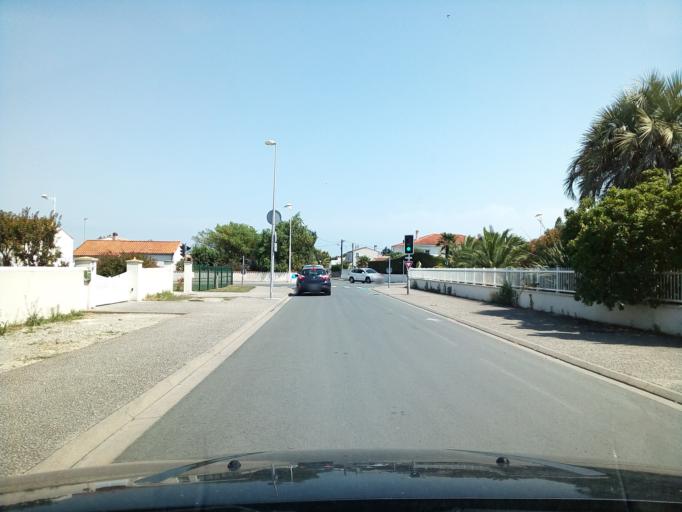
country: FR
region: Poitou-Charentes
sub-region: Departement de la Charente-Maritime
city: Dolus-d'Oleron
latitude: 45.9383
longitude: -1.3044
